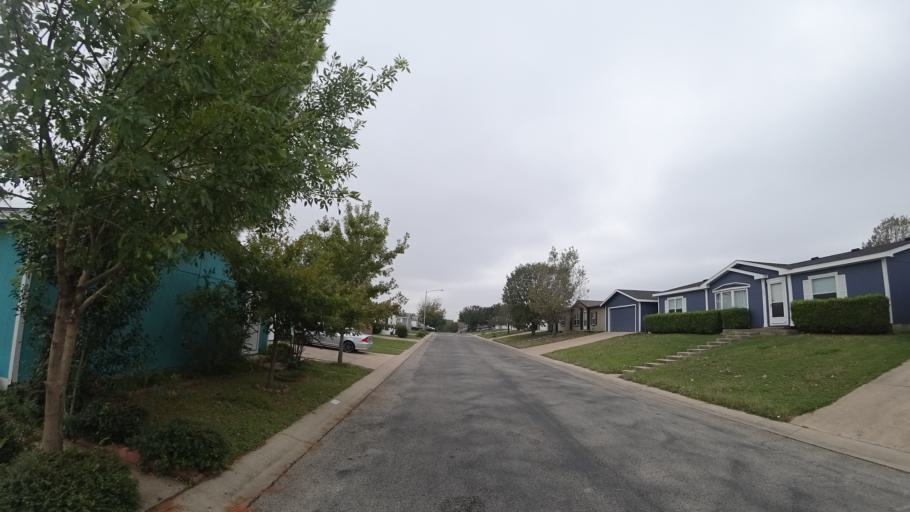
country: US
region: Texas
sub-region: Travis County
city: Pflugerville
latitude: 30.3903
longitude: -97.6402
